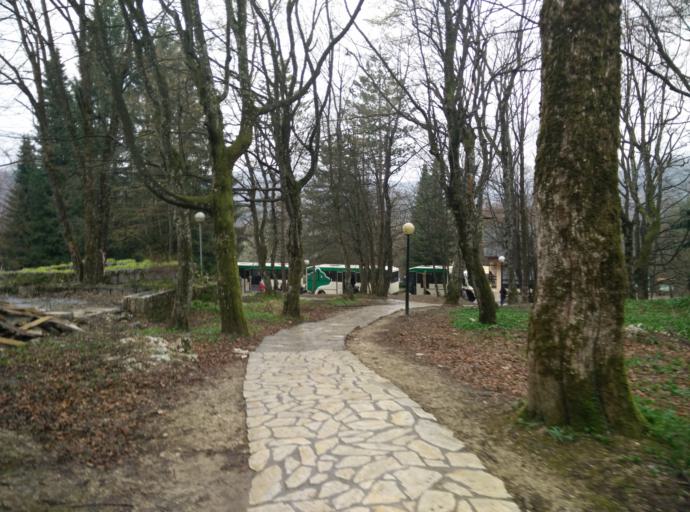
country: HR
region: Licko-Senjska
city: Jezerce
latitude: 44.8828
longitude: 15.6192
